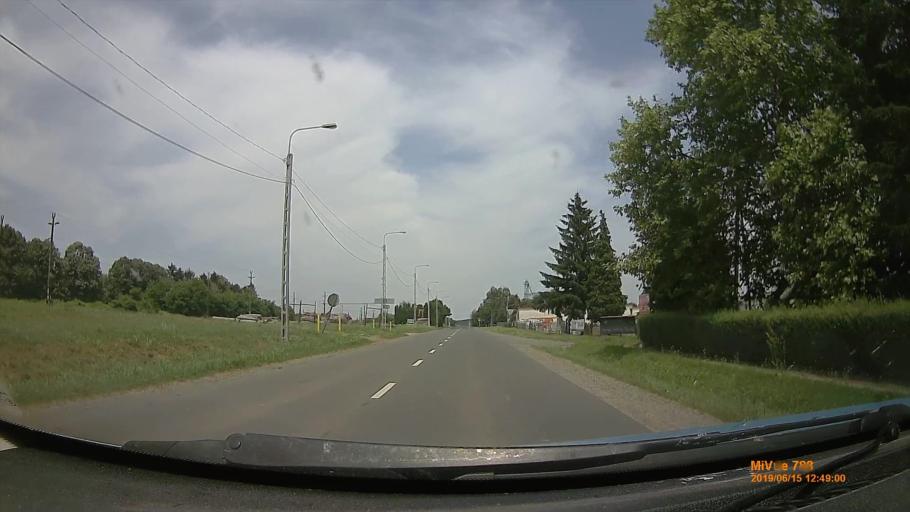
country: HU
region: Baranya
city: Sasd
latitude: 46.2601
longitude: 18.1057
